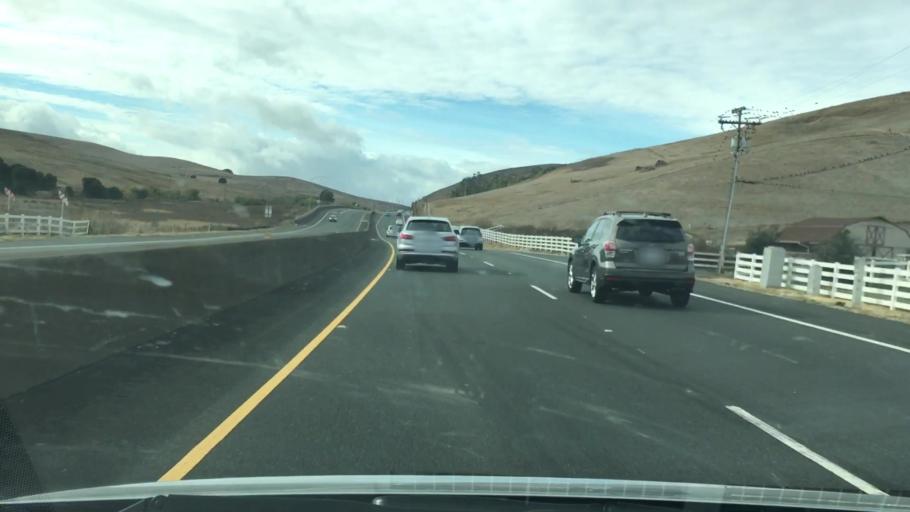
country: US
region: California
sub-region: Solano County
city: Green Valley
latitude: 38.2085
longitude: -122.1864
